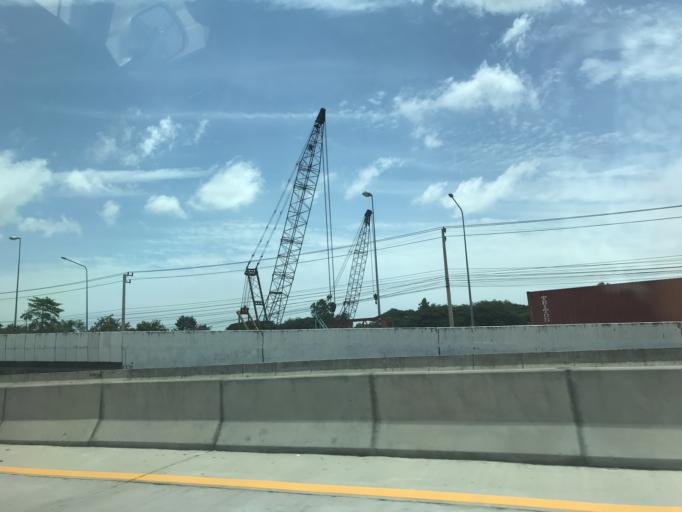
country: TH
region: Chon Buri
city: Ban Talat Bueng
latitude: 13.1139
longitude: 100.9642
